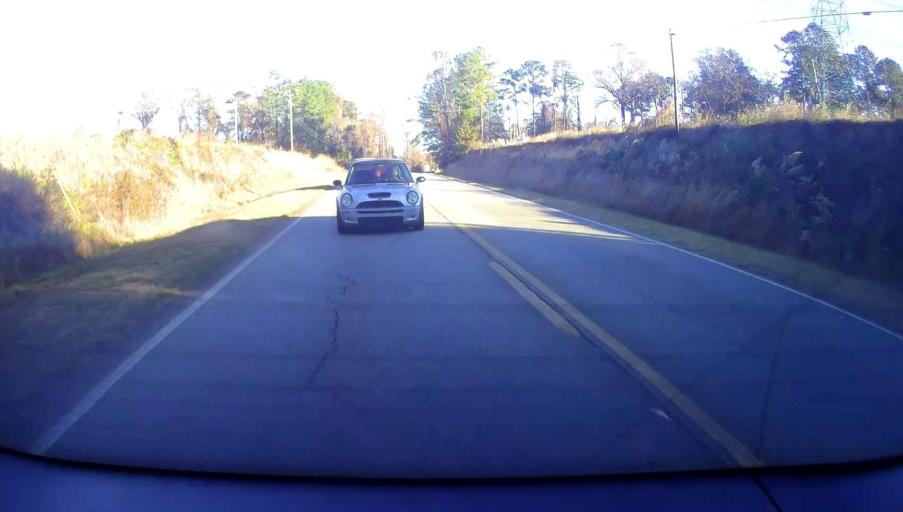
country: US
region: Georgia
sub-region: Houston County
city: Centerville
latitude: 32.6090
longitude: -83.7131
